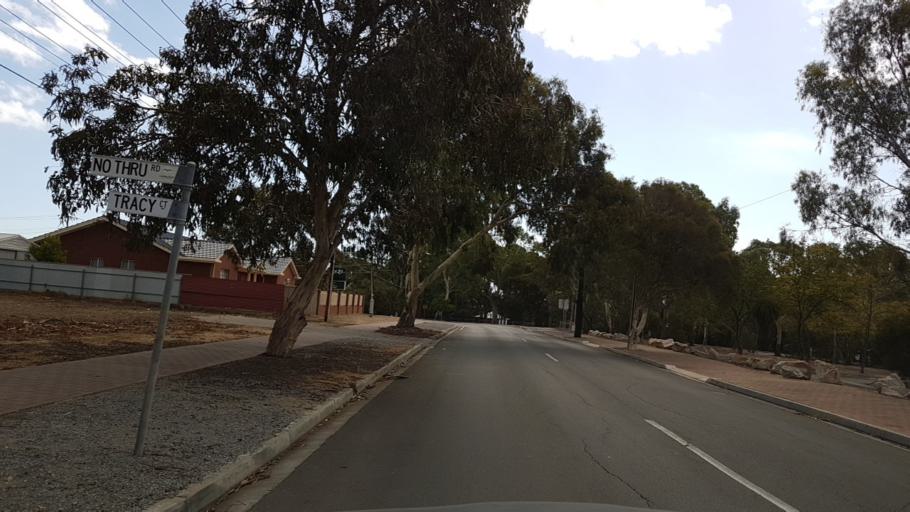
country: AU
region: South Australia
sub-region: Campbelltown
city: Athelstone
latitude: -34.8754
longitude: 138.6920
